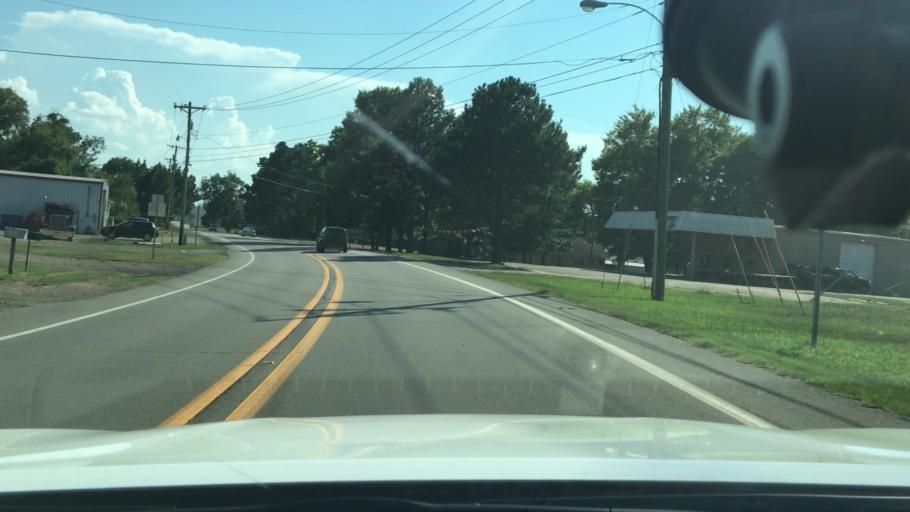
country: US
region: Arkansas
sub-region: Johnson County
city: Clarksville
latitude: 35.4722
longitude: -93.5134
